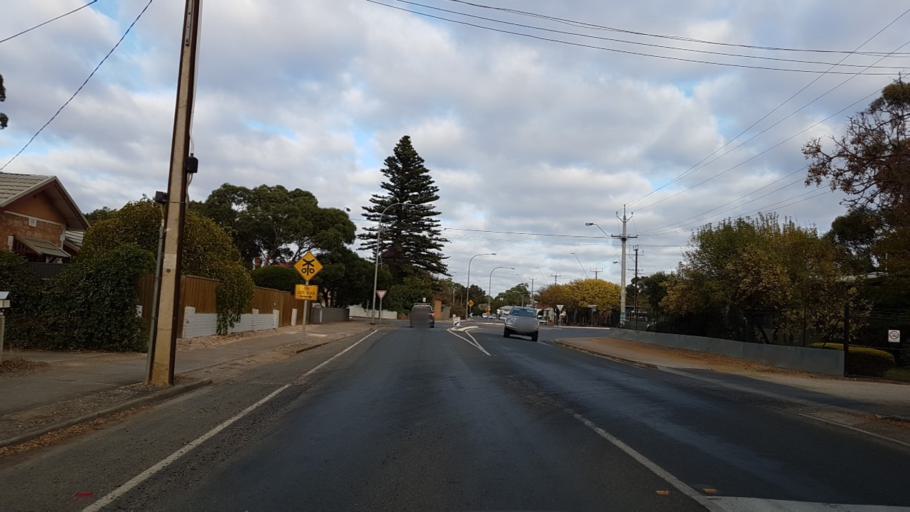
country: AU
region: South Australia
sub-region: Alexandrina
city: Strathalbyn
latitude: -35.2580
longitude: 138.8991
